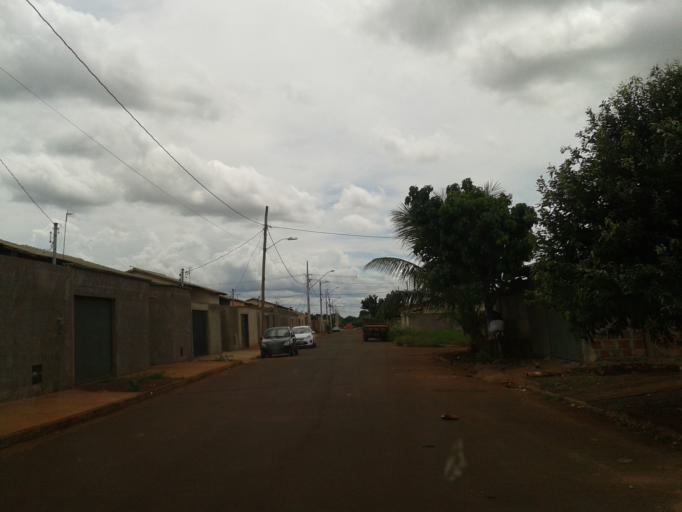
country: BR
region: Minas Gerais
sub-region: Centralina
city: Centralina
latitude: -18.5885
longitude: -49.2053
